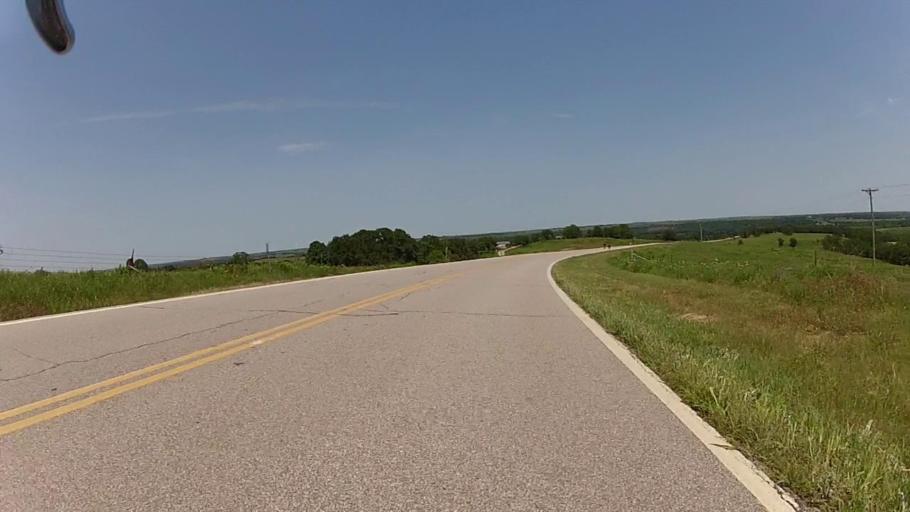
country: US
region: Kansas
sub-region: Chautauqua County
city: Sedan
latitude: 37.1142
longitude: -96.2424
